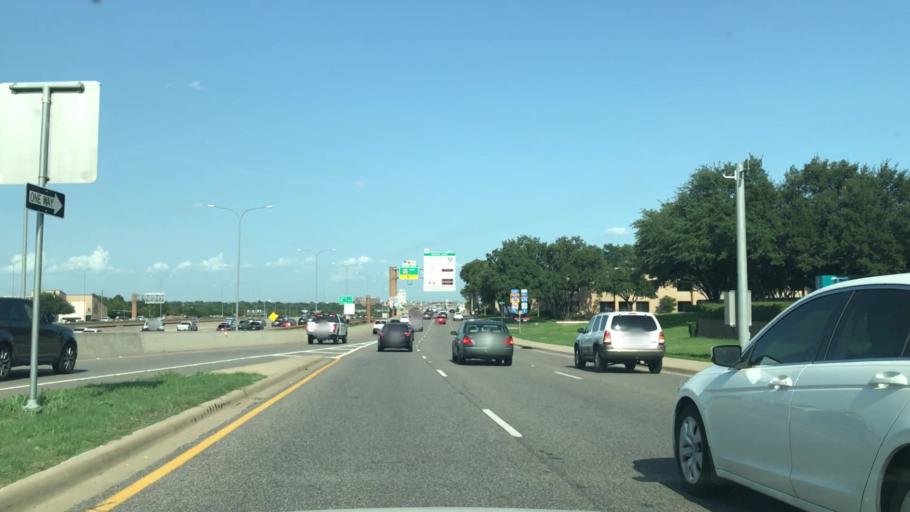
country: US
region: Texas
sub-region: Dallas County
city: Addison
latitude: 32.9237
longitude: -96.7982
